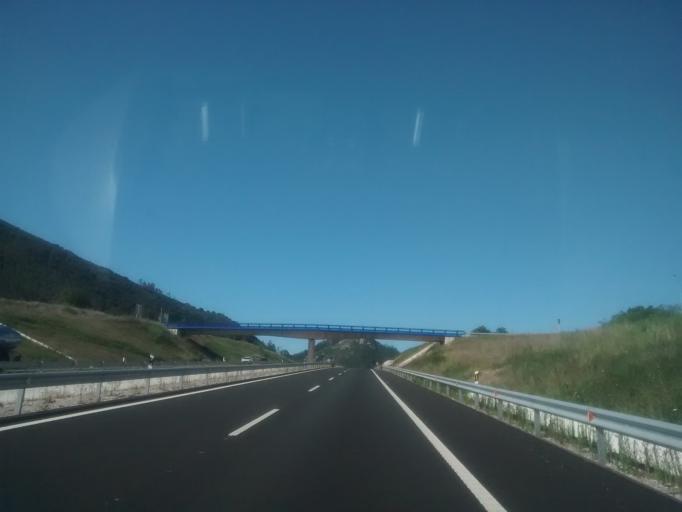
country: ES
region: Cantabria
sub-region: Provincia de Cantabria
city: Lierganes
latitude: 43.3657
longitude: -3.7585
